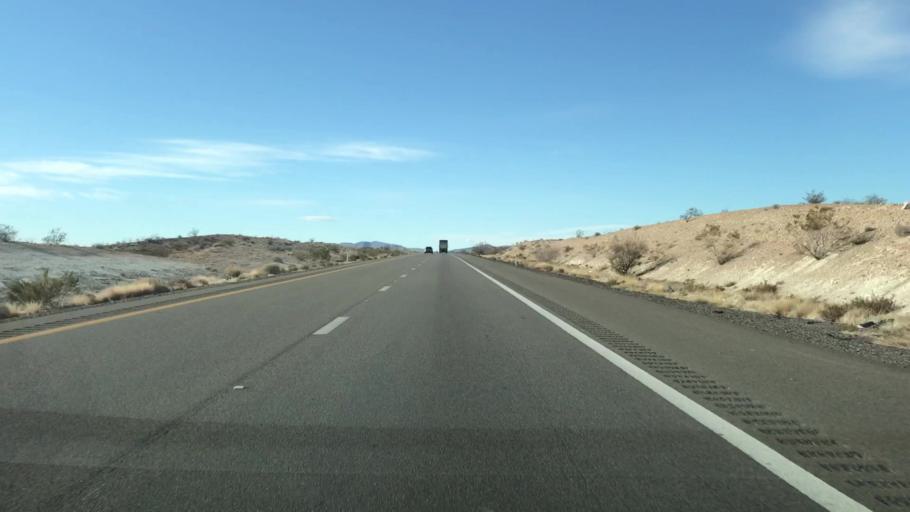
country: US
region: Nevada
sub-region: Clark County
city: Moapa Town
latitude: 36.5382
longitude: -114.7162
